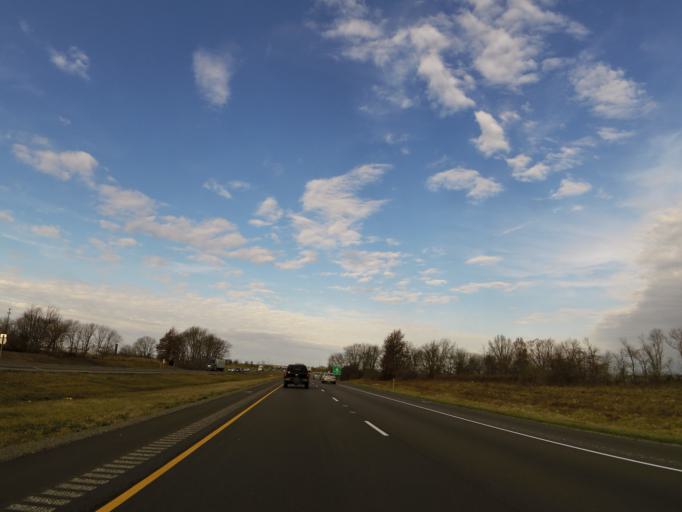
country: US
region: Illinois
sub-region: Washington County
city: Okawville
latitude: 38.4355
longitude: -89.5217
